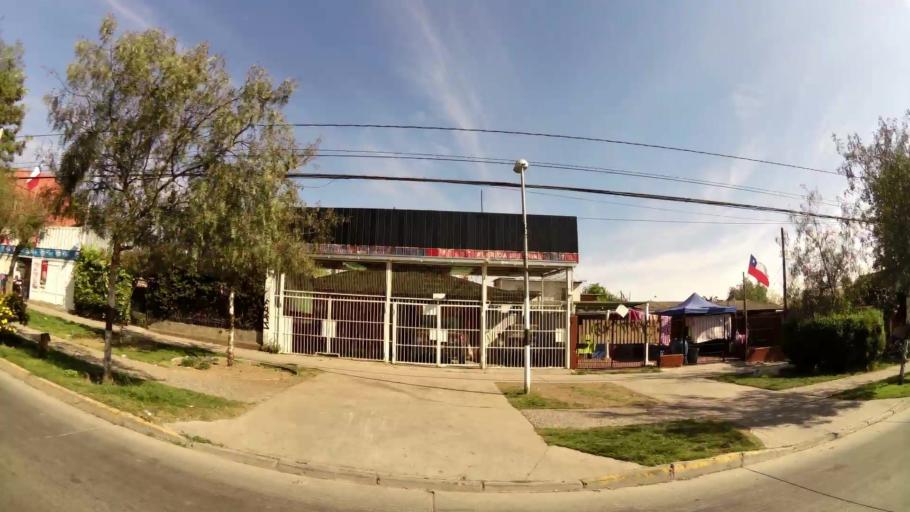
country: CL
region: Santiago Metropolitan
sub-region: Provincia de Santiago
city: Villa Presidente Frei, Nunoa, Santiago, Chile
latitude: -33.4724
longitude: -70.5609
